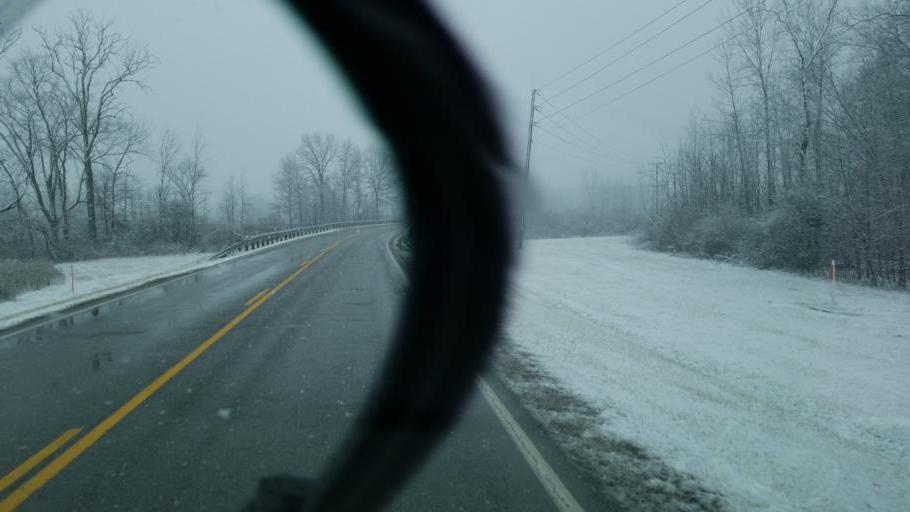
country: US
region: Ohio
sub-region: Champaign County
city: North Lewisburg
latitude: 40.2787
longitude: -83.4892
